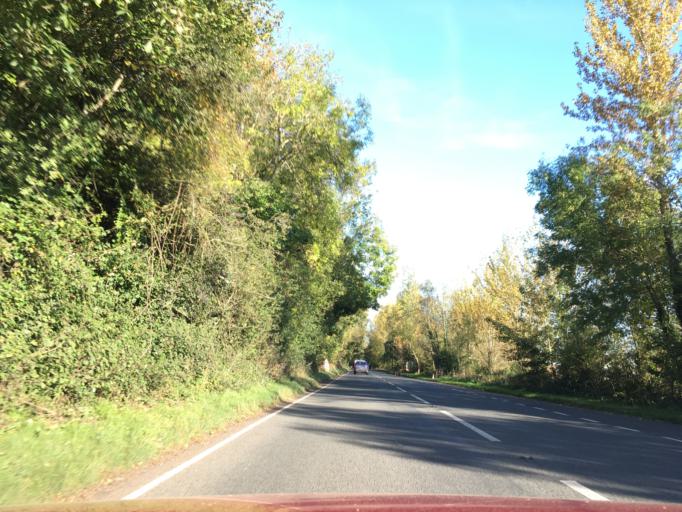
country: GB
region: England
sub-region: Herefordshire
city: Clifford
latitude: 52.1210
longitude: -3.0834
